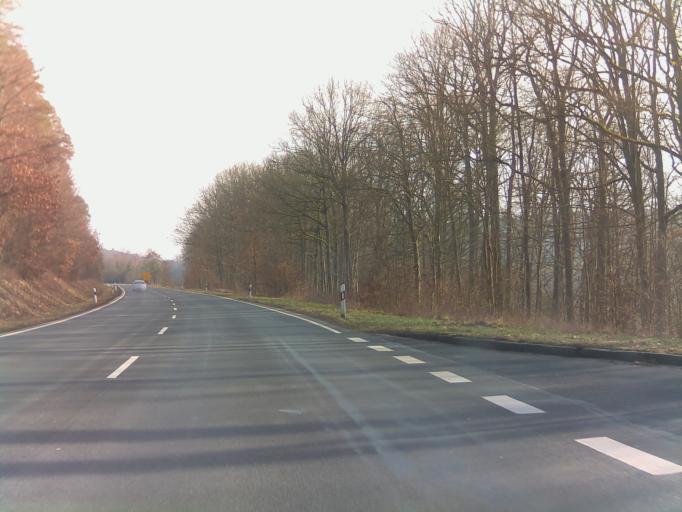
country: DE
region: Bavaria
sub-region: Regierungsbezirk Unterfranken
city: Hohenroth
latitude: 50.3613
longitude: 10.1290
